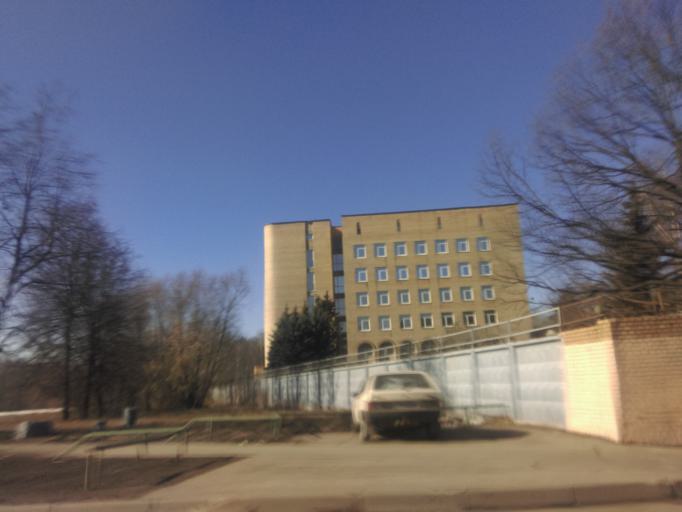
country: RU
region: Moskovskaya
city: Mosrentgen
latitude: 55.6356
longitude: 37.4728
